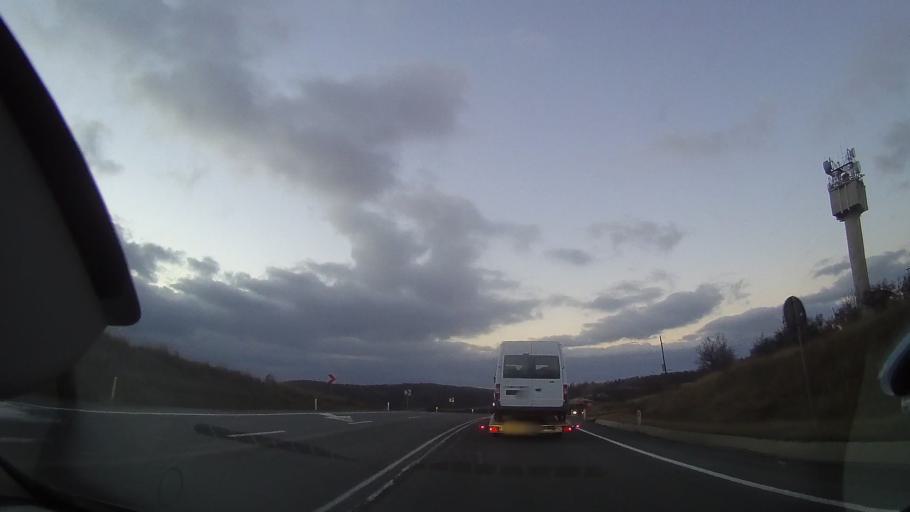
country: RO
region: Cluj
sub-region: Comuna Izvoru Crisului
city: Izvoru Crisului
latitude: 46.8261
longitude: 23.1546
